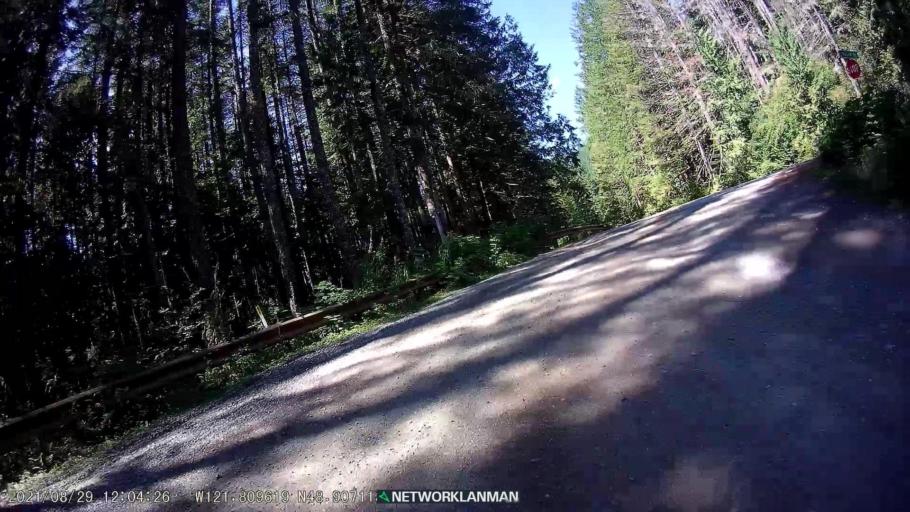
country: CA
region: British Columbia
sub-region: Fraser Valley Regional District
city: Chilliwack
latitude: 48.9069
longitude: -121.8088
